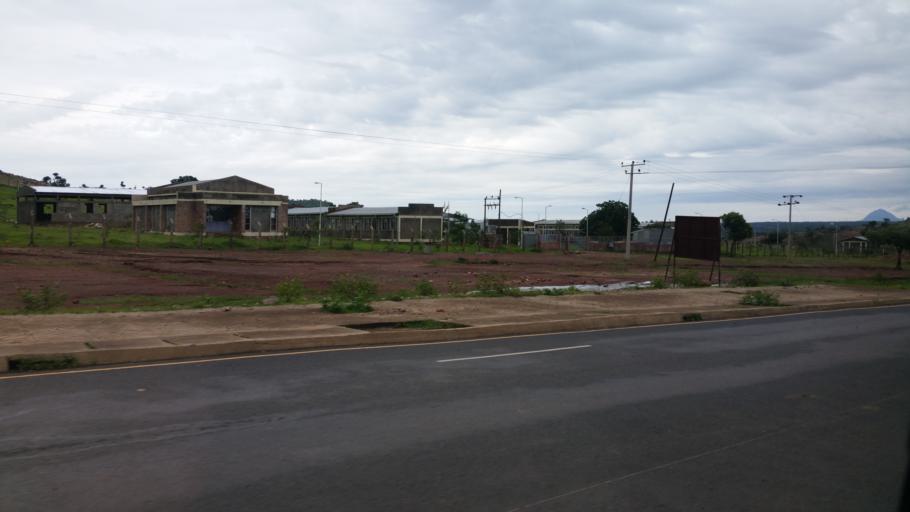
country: ET
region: Amhara
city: Debark'
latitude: 13.5963
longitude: 38.1455
